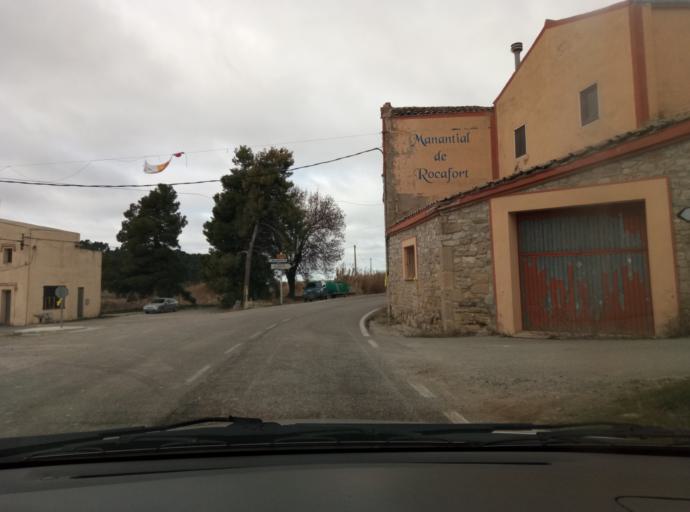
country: ES
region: Catalonia
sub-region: Provincia de Lleida
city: Nalec
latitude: 41.5580
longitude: 1.0932
